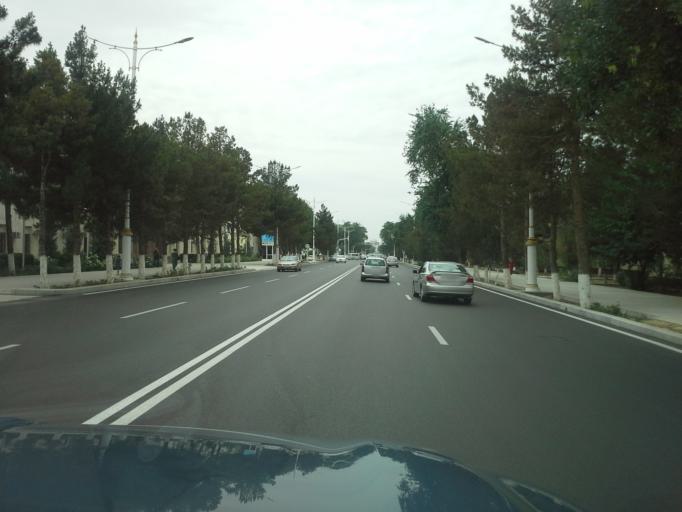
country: TM
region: Ahal
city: Ashgabat
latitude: 37.9487
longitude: 58.3758
